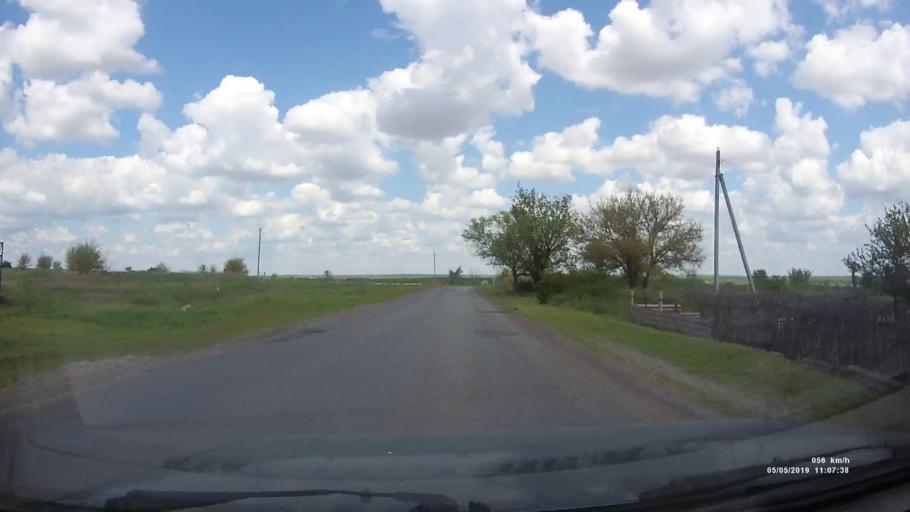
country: RU
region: Rostov
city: Ust'-Donetskiy
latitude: 47.7271
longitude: 40.9141
